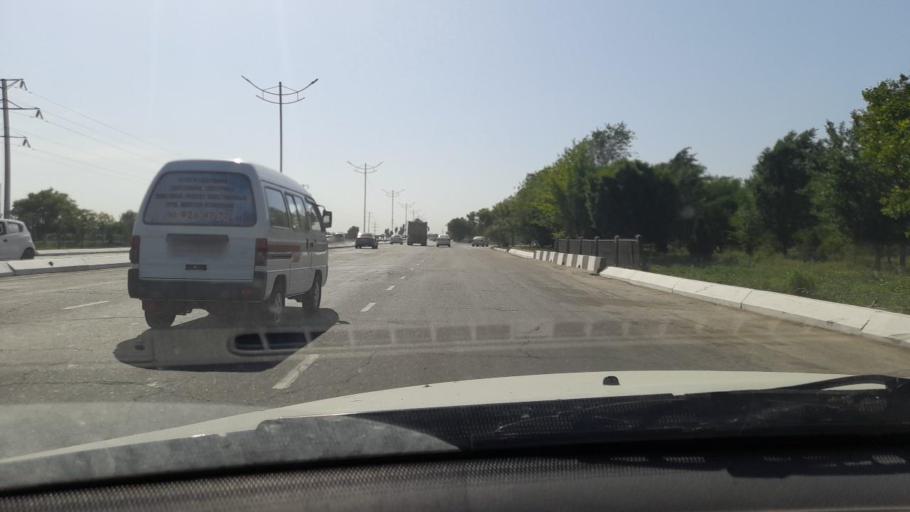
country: UZ
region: Bukhara
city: Bukhara
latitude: 39.7992
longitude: 64.4345
